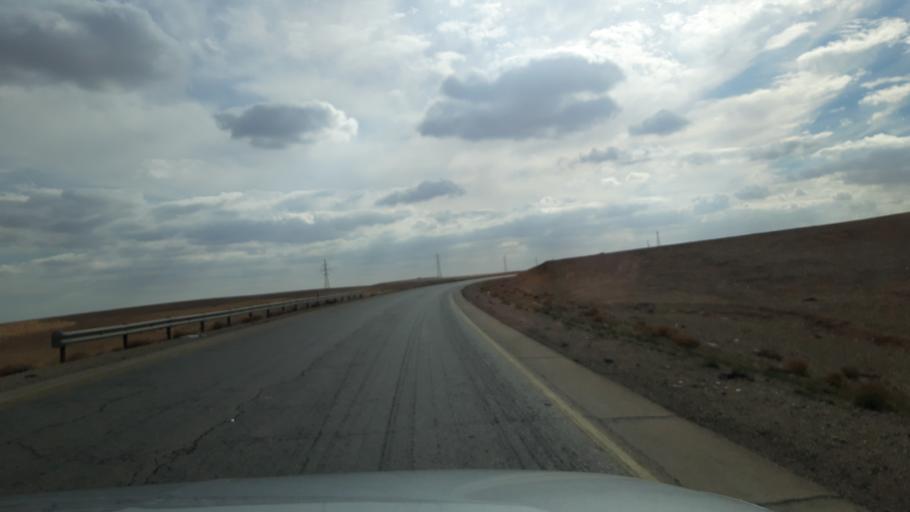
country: JO
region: Amman
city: Al Azraq ash Shamali
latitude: 31.7442
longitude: 36.5354
